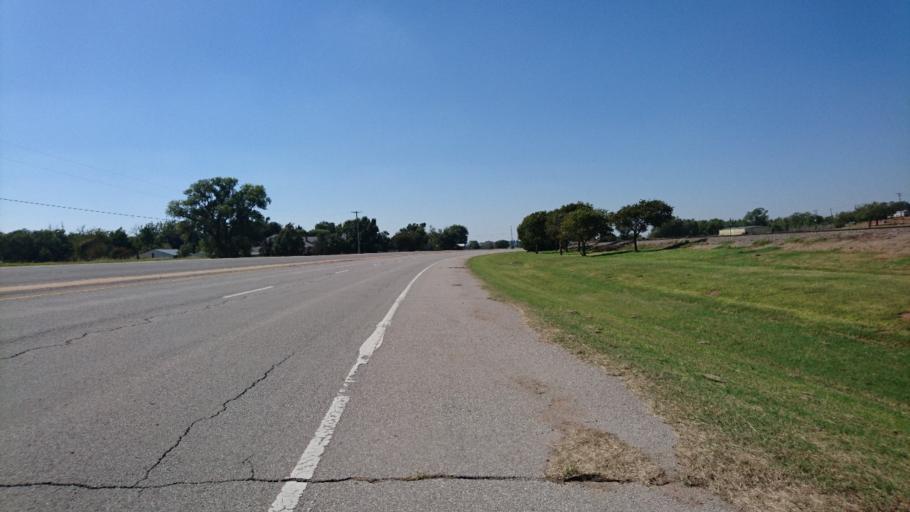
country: US
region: Oklahoma
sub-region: Custer County
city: Clinton
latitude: 35.5140
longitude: -98.9378
